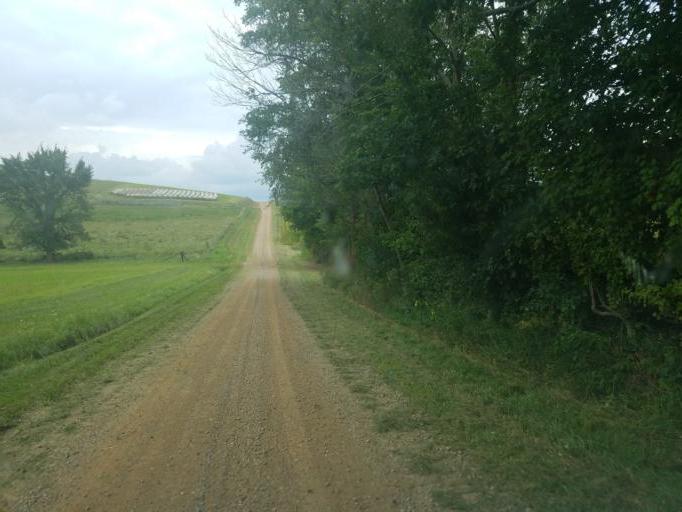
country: US
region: Ohio
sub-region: Knox County
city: Danville
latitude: 40.5188
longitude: -82.3053
